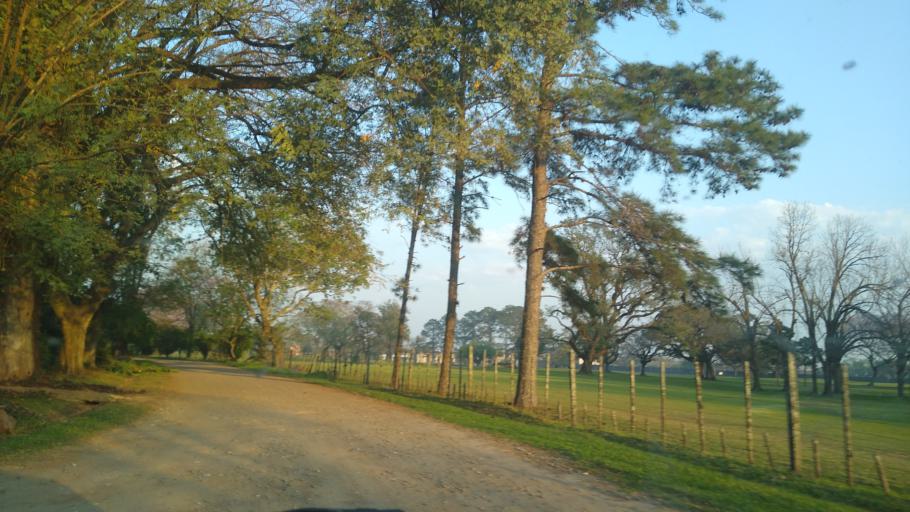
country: AR
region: Chaco
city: Barranqueras
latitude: -27.4662
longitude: -58.9553
